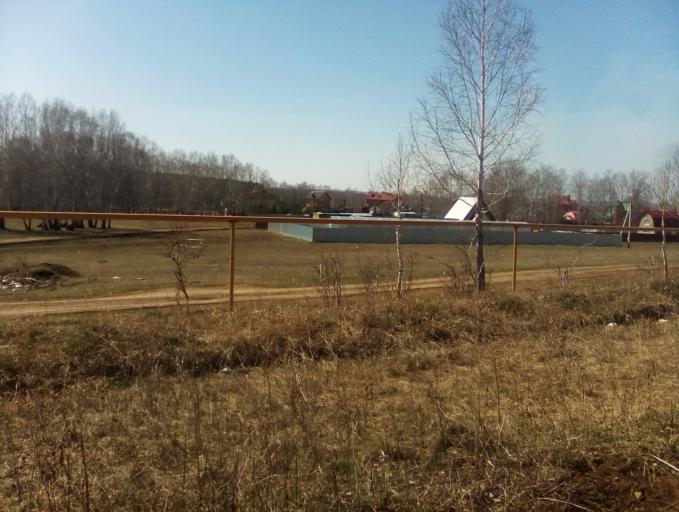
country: RU
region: Chelyabinsk
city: Sargazy
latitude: 55.0322
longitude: 61.2406
